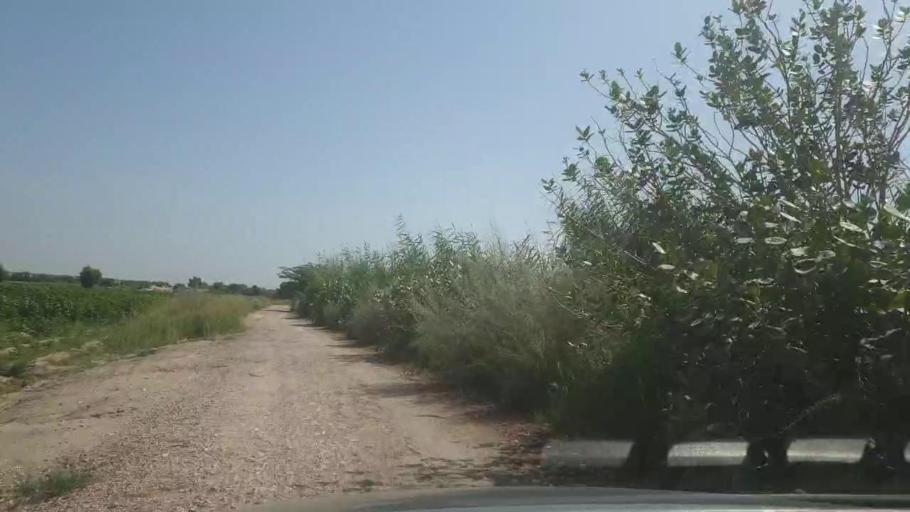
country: PK
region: Sindh
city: Rohri
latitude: 27.4074
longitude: 69.0854
